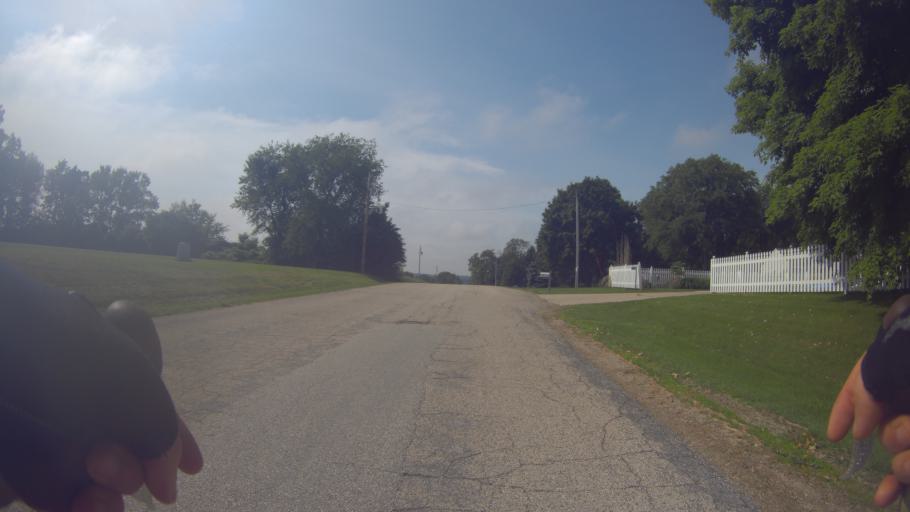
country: US
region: Wisconsin
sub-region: Dane County
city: Stoughton
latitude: 42.9627
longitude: -89.1810
